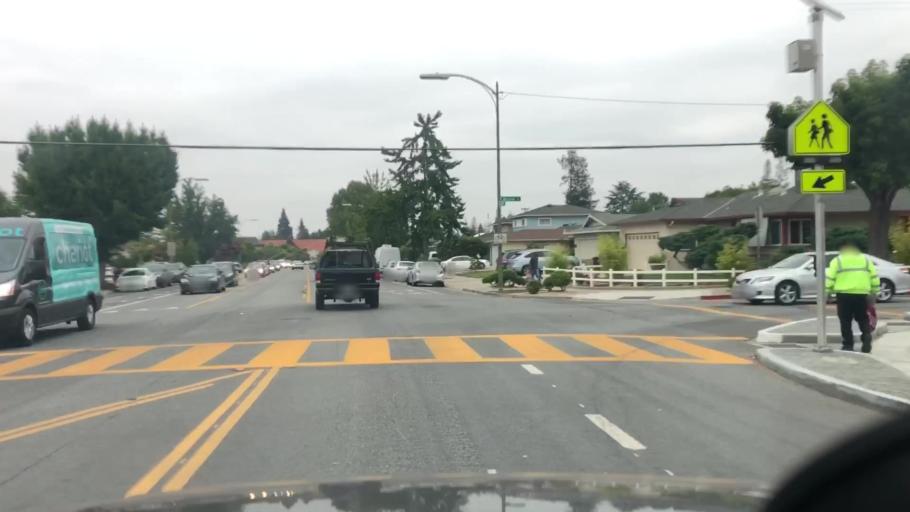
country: US
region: California
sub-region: Santa Clara County
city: Cupertino
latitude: 37.3117
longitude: -121.9905
